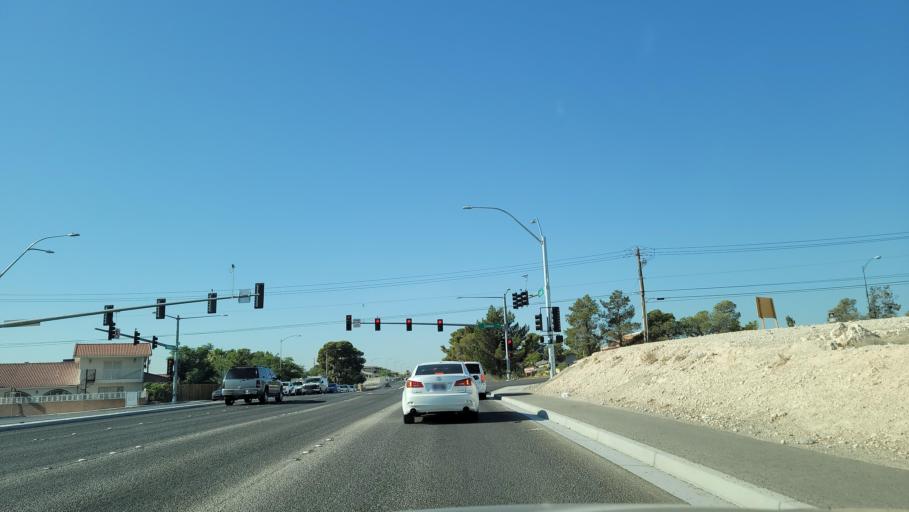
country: US
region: Nevada
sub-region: Clark County
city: Las Vegas
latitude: 36.2254
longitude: -115.1799
